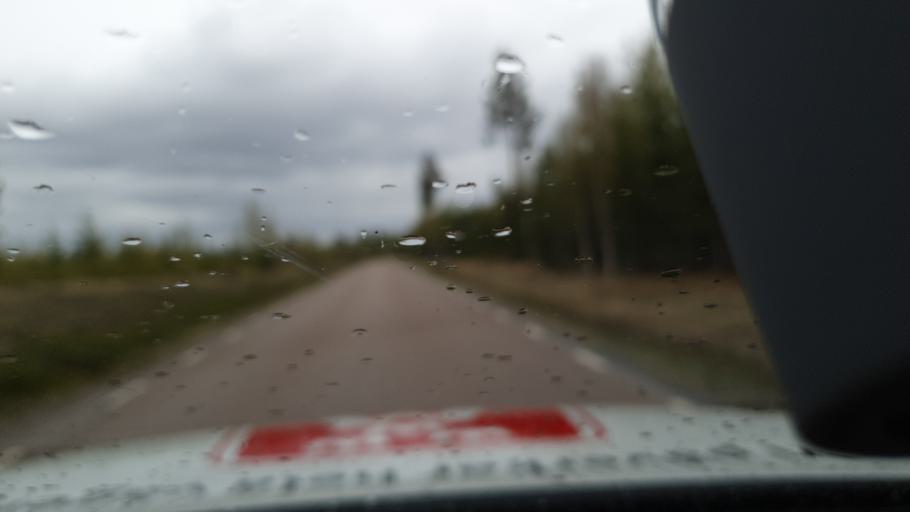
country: SE
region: Jaemtland
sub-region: OEstersunds Kommun
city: Lit
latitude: 63.3052
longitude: 14.9141
